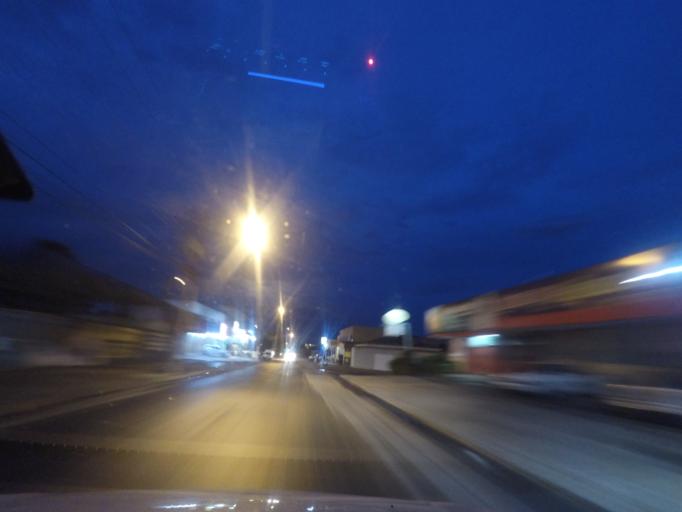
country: BR
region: Goias
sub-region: Goiania
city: Goiania
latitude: -16.7068
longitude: -49.3245
